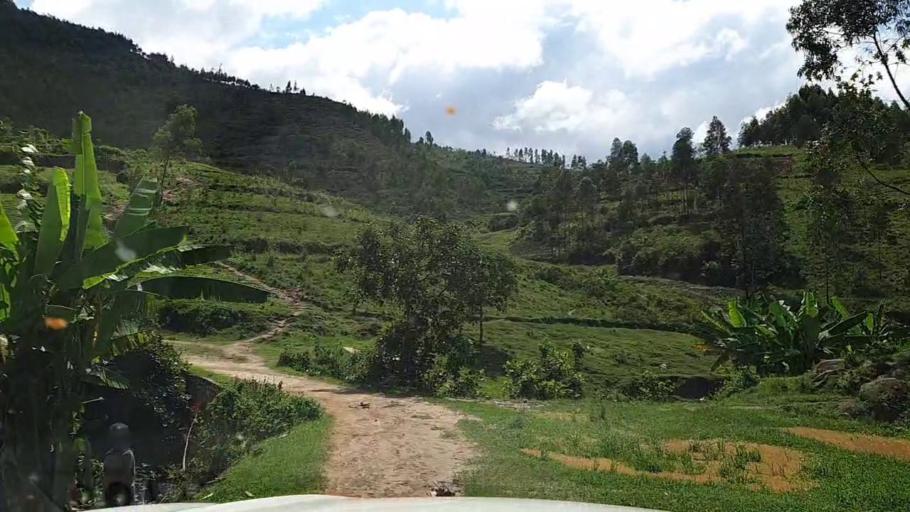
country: RW
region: Southern Province
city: Gikongoro
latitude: -2.3616
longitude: 29.5317
